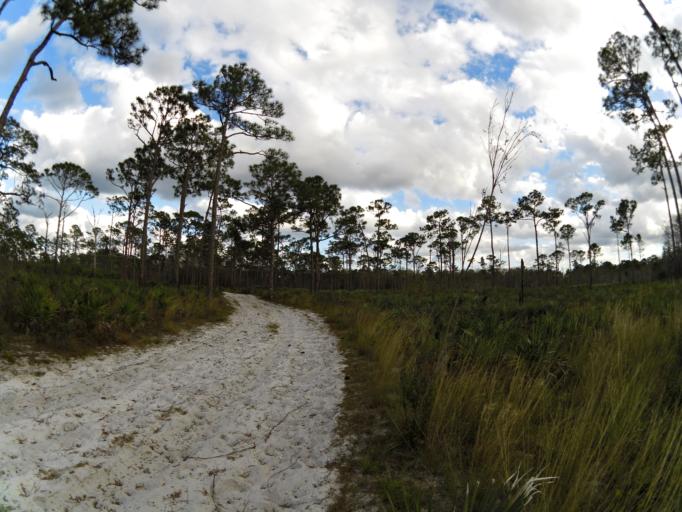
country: US
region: Florida
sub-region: Palm Beach County
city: Tequesta
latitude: 27.0096
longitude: -80.1422
